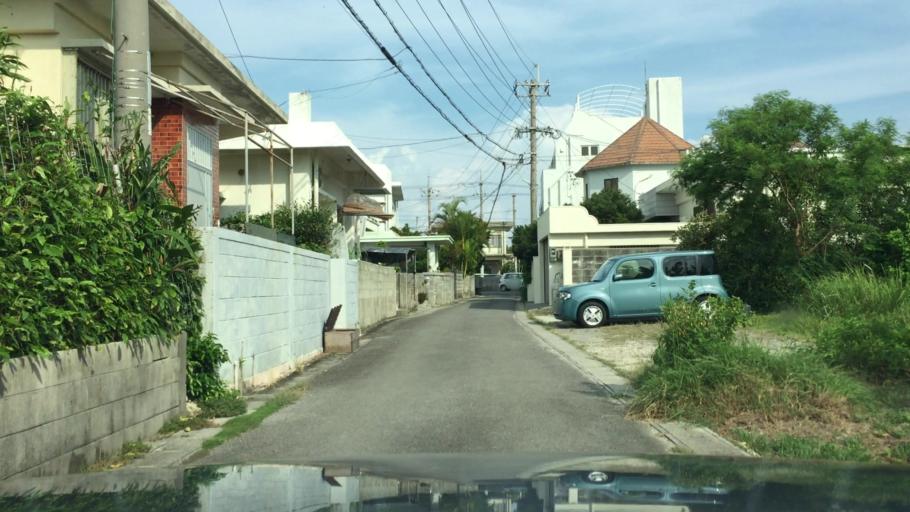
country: JP
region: Okinawa
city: Ishigaki
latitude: 24.3484
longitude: 124.1618
